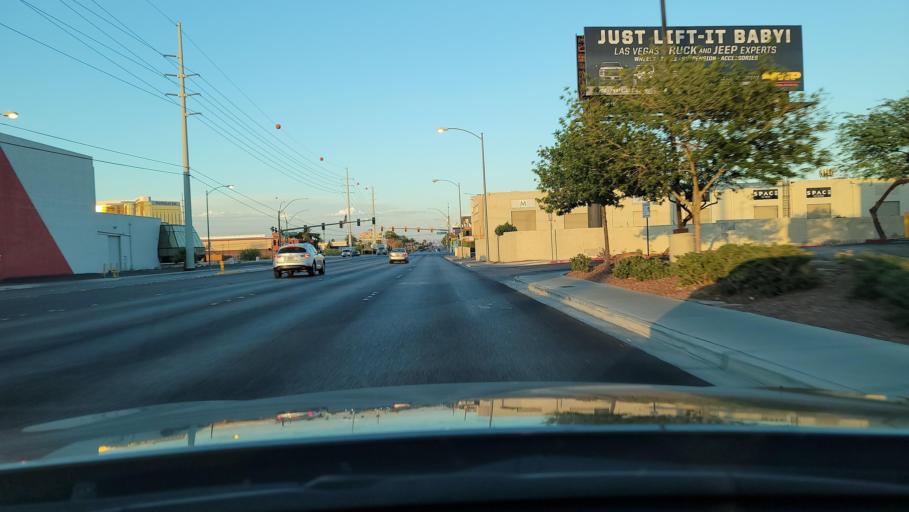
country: US
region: Nevada
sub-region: Clark County
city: Paradise
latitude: 36.0862
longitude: -115.1915
